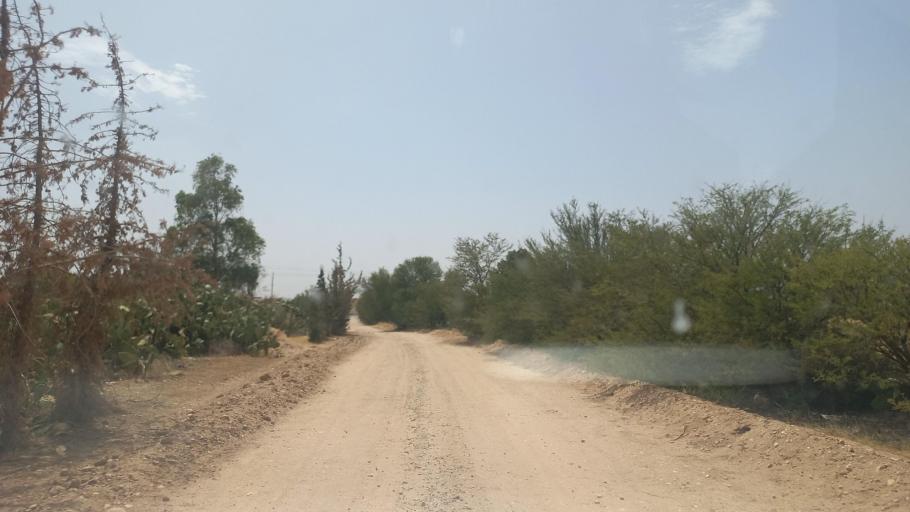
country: TN
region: Al Qasrayn
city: Kasserine
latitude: 35.2528
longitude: 9.0082
